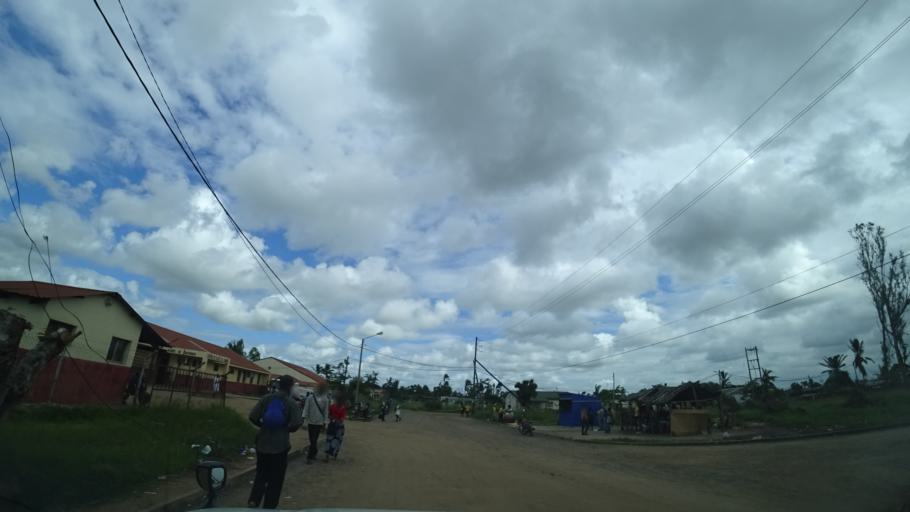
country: MZ
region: Sofala
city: Dondo
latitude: -19.6179
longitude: 34.7415
